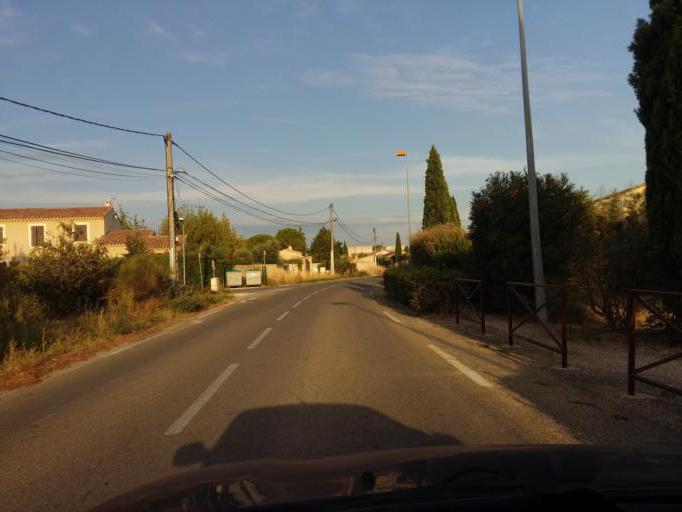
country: FR
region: Provence-Alpes-Cote d'Azur
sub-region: Departement du Vaucluse
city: Monteux
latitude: 44.0346
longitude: 4.9839
